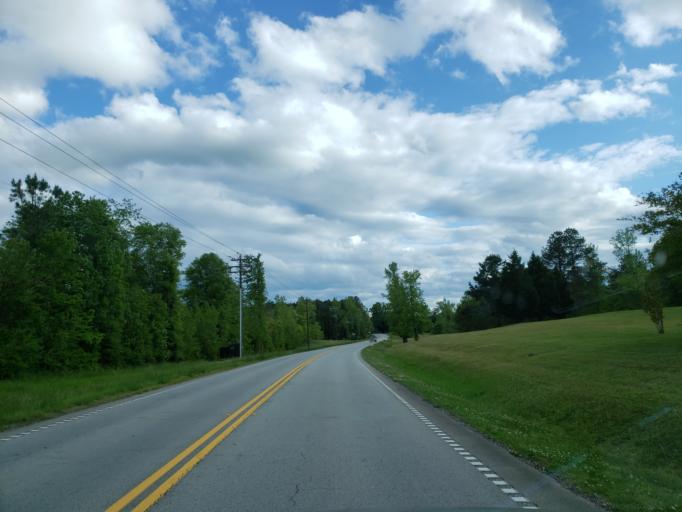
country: US
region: Georgia
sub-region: Haralson County
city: Tallapoosa
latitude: 33.8362
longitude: -85.2929
